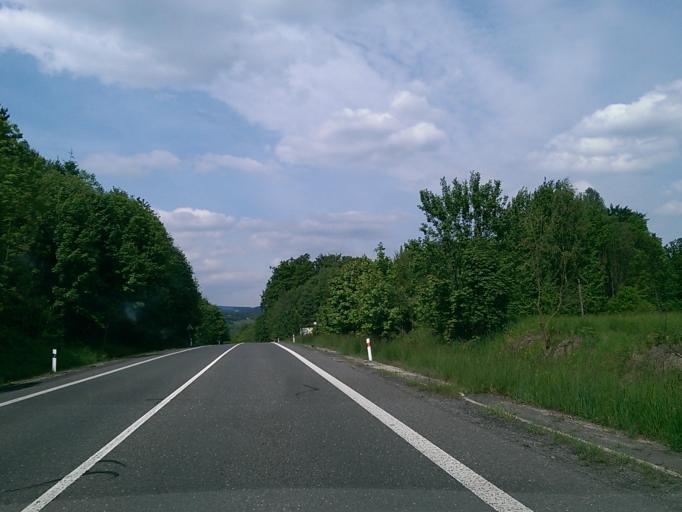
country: CZ
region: Liberecky
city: Mala Skala
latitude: 50.6308
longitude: 15.1862
